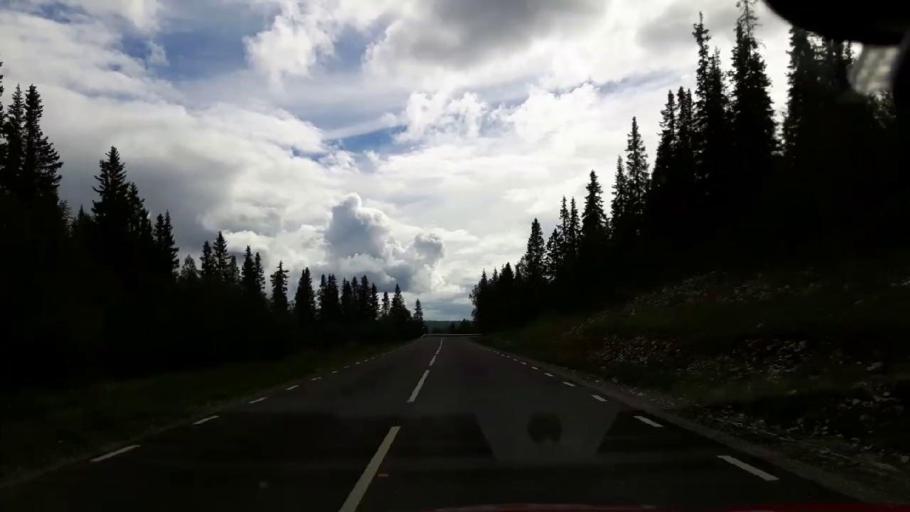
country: NO
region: Nord-Trondelag
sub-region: Royrvik
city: Royrvik
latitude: 64.8076
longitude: 14.0698
